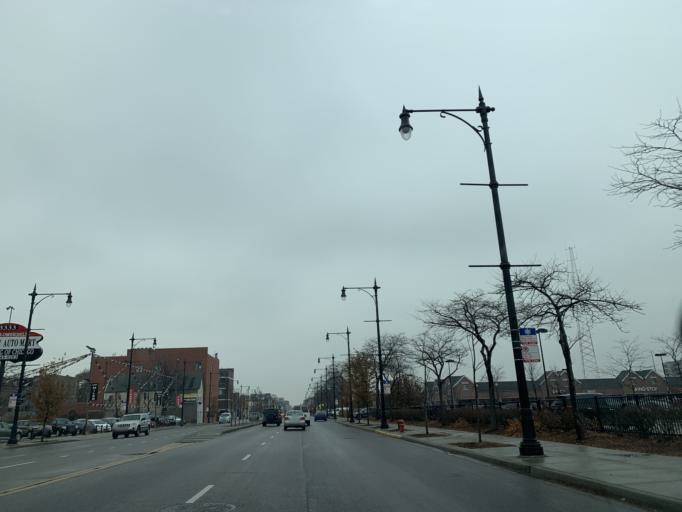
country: US
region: Illinois
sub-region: Cook County
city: Lincolnwood
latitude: 41.9427
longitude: -87.6882
